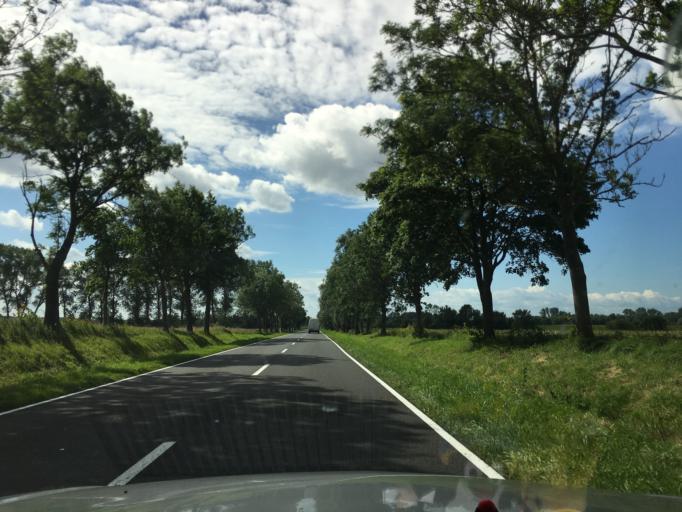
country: PL
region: West Pomeranian Voivodeship
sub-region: Powiat kamienski
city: Kamien Pomorski
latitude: 53.9317
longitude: 14.8119
